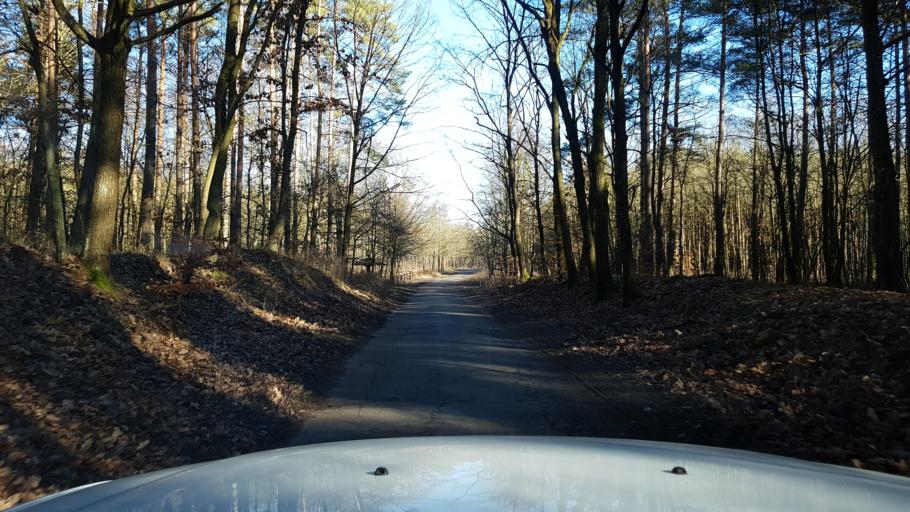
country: PL
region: West Pomeranian Voivodeship
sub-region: Powiat pyrzycki
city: Lipiany
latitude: 53.0193
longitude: 15.0047
